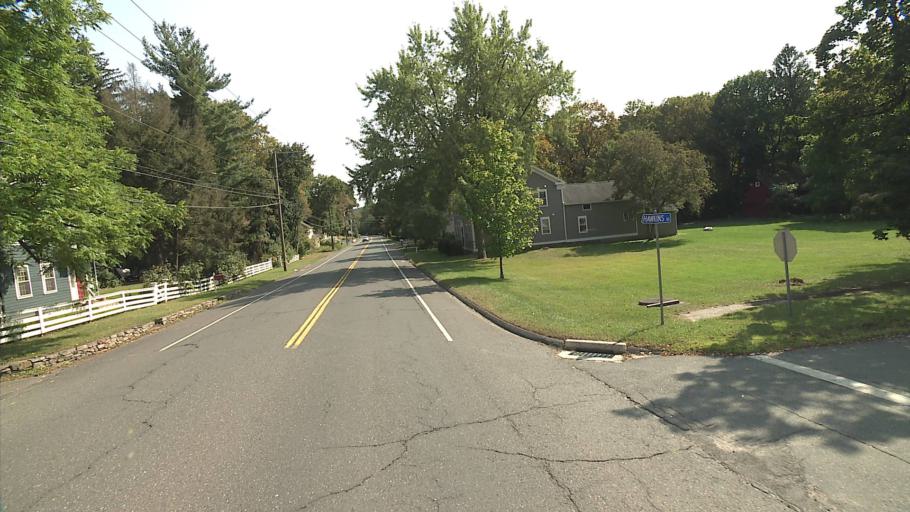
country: US
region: Connecticut
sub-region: New Haven County
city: Heritage Village
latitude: 41.4704
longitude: -73.2511
